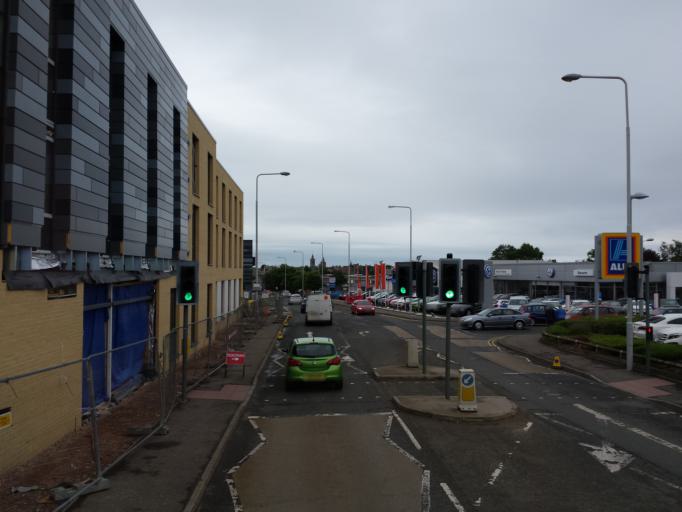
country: GB
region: Scotland
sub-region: Fife
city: Saint Andrews
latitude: 56.3310
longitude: -2.8047
